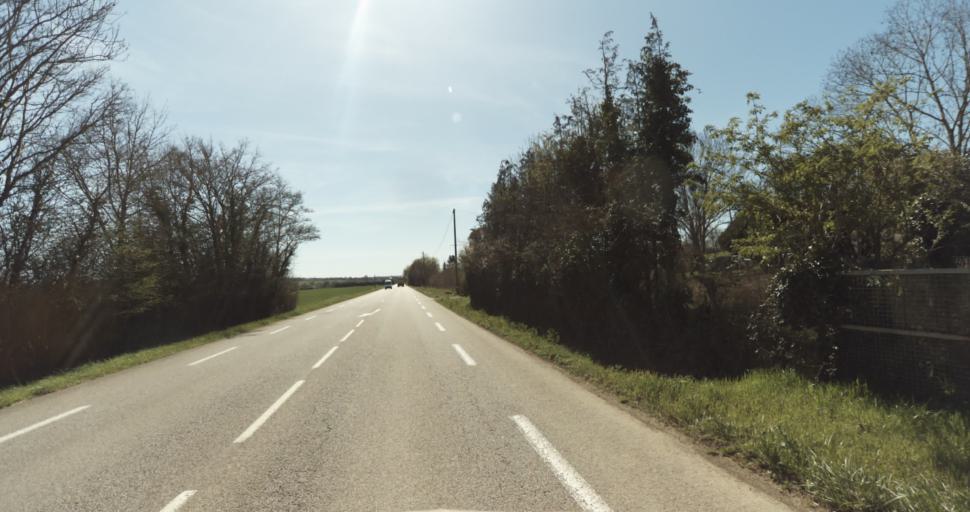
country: FR
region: Lower Normandy
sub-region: Departement du Calvados
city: Saint-Pierre-sur-Dives
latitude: 49.0527
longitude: -0.0110
